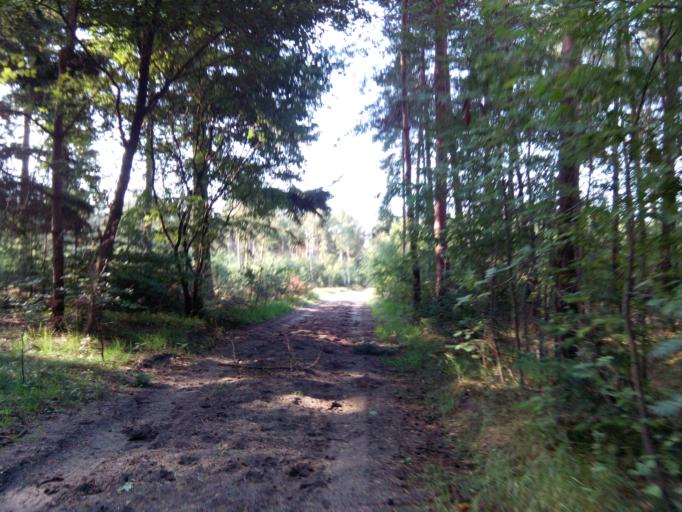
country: NL
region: Utrecht
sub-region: Gemeente Utrechtse Heuvelrug
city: Maarn
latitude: 52.1077
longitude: 5.3640
